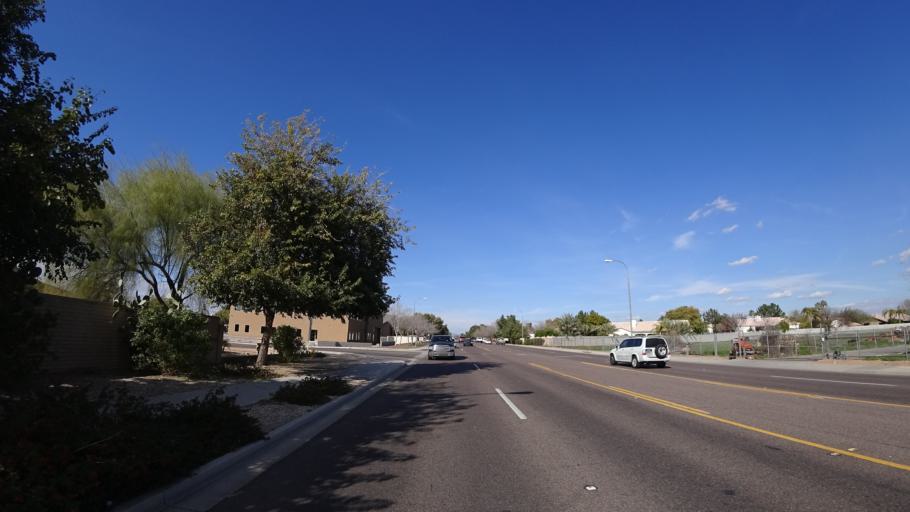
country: US
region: Arizona
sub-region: Maricopa County
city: Peoria
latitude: 33.6188
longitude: -112.2201
